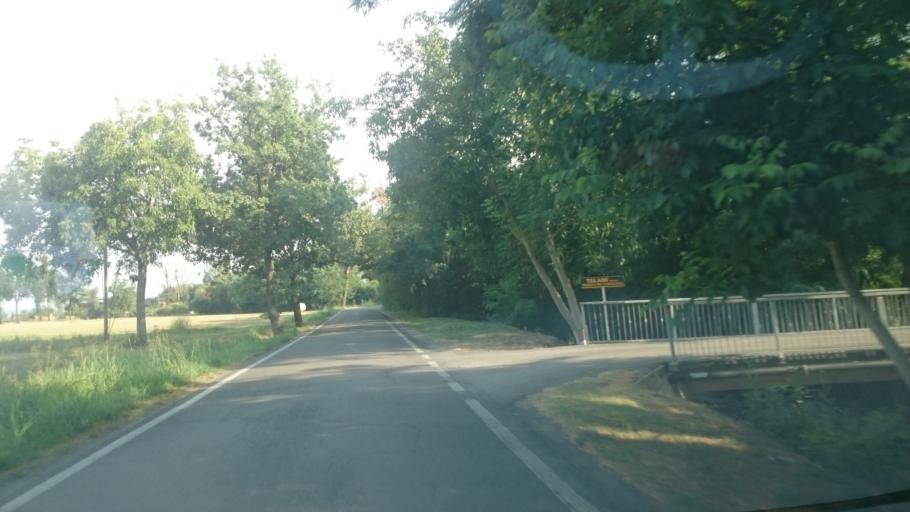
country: IT
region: Emilia-Romagna
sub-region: Provincia di Reggio Emilia
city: Arceto
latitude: 44.6044
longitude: 10.7259
